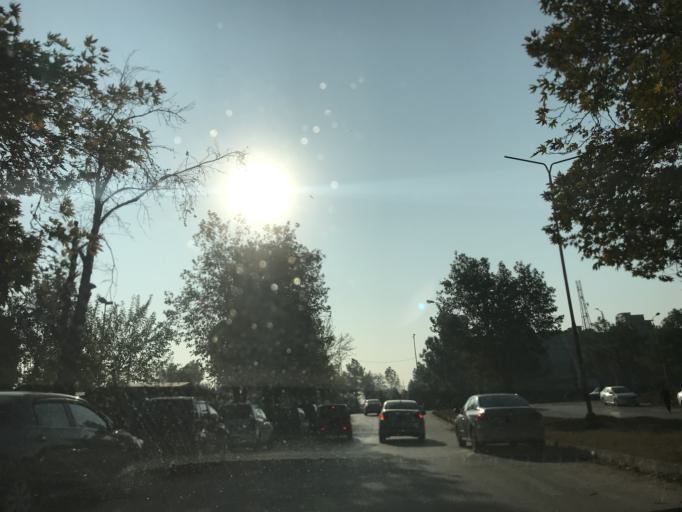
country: PK
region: Islamabad
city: Islamabad
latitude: 33.7146
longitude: 73.0627
